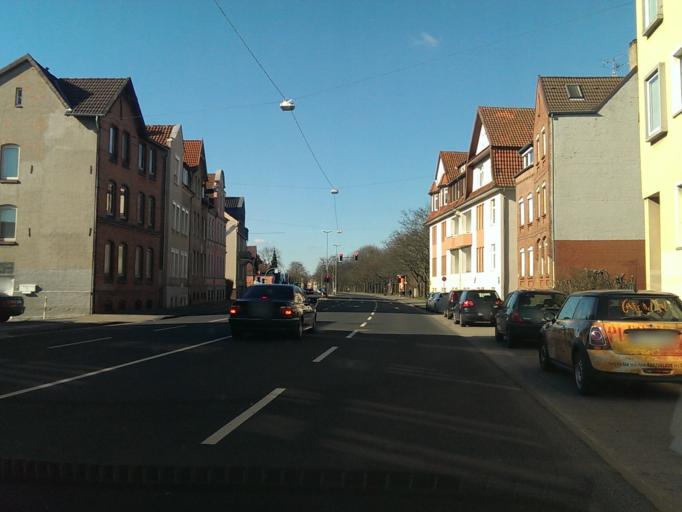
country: DE
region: Lower Saxony
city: Hildesheim
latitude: 52.1444
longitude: 9.9396
